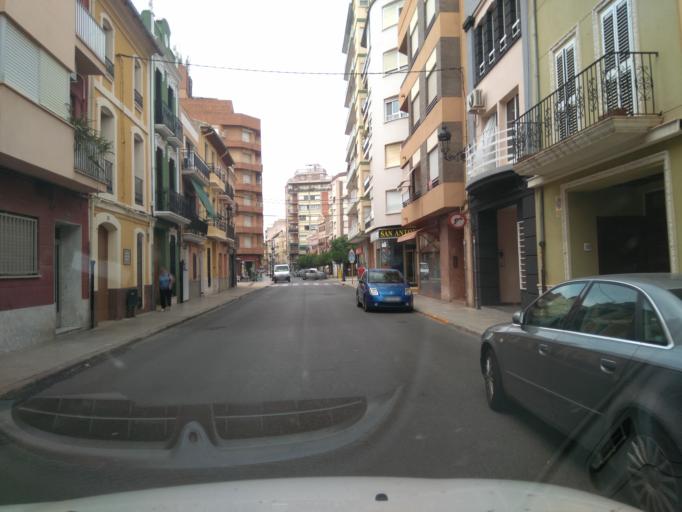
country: ES
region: Valencia
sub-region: Provincia de Valencia
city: Carcaixent
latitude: 39.1204
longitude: -0.4467
